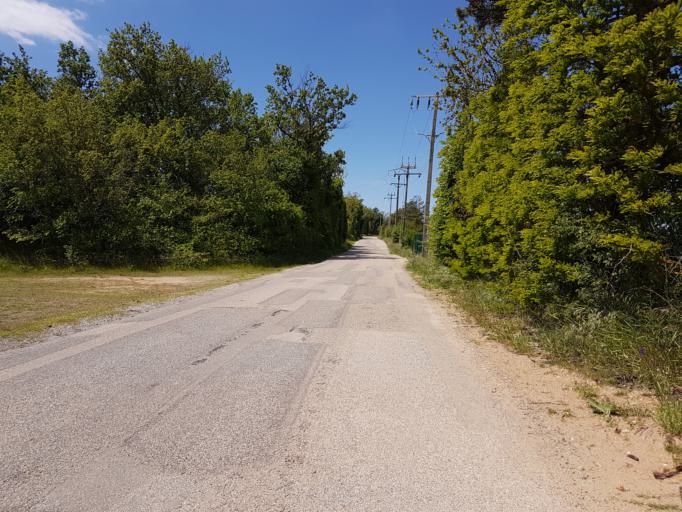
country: FR
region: Rhone-Alpes
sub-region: Departement de l'Isere
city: Saint-Romain-de-Jalionas
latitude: 45.7630
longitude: 5.2296
